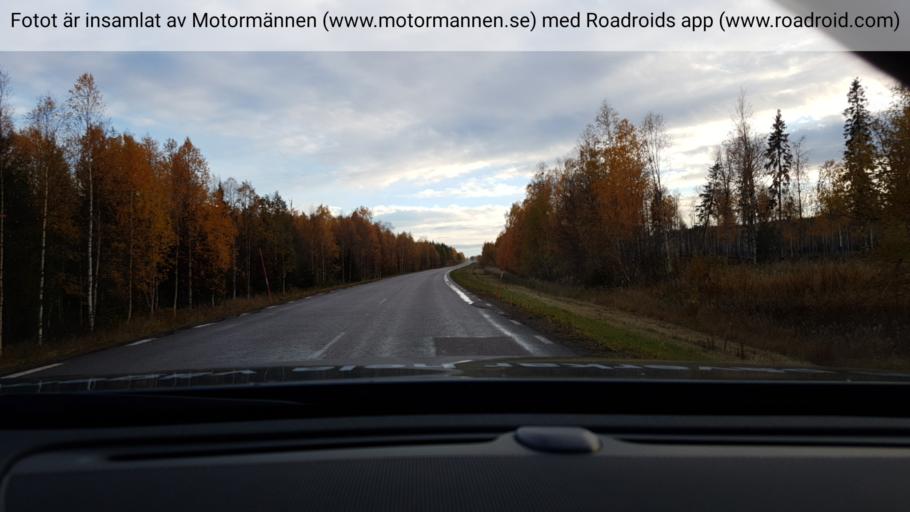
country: SE
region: Norrbotten
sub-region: Overkalix Kommun
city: OEverkalix
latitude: 66.8481
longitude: 22.7588
